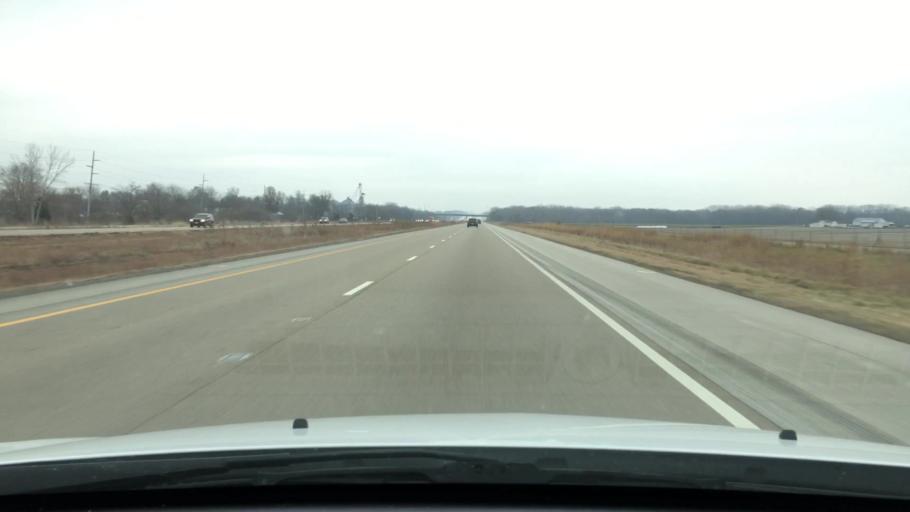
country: US
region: Illinois
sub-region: Logan County
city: Atlanta
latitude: 40.2113
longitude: -89.2885
